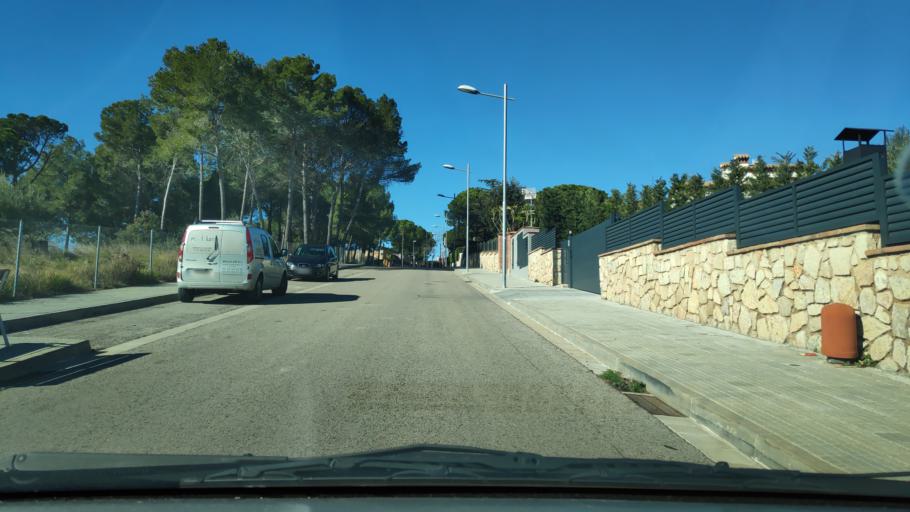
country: ES
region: Catalonia
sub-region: Provincia de Barcelona
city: Matadepera
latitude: 41.5922
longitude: 2.0299
